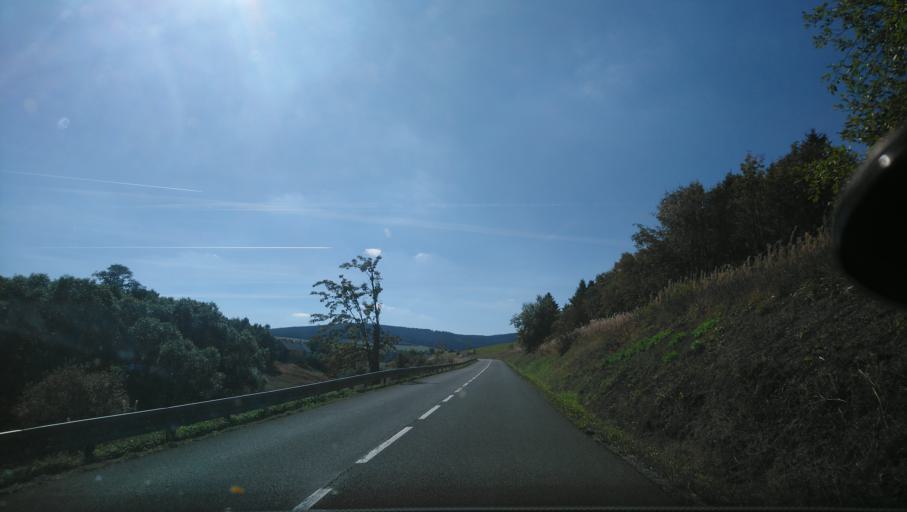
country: DE
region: Saxony
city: Kurort Oberwiesenthal
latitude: 50.4219
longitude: 12.9969
